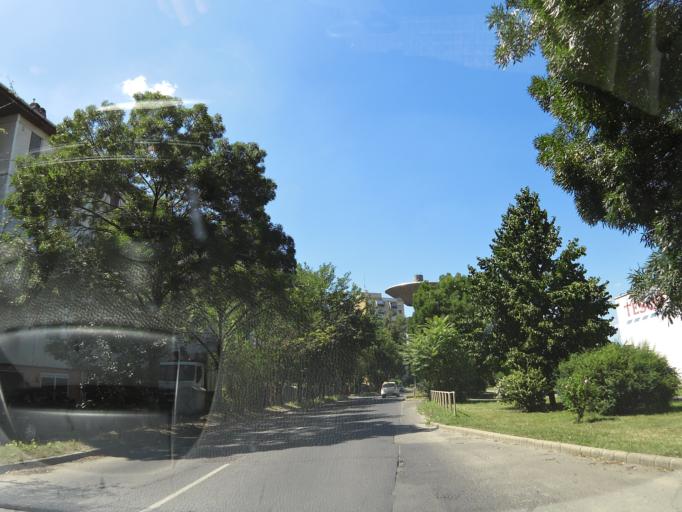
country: HU
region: Csongrad
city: Szeged
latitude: 46.2673
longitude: 20.1381
